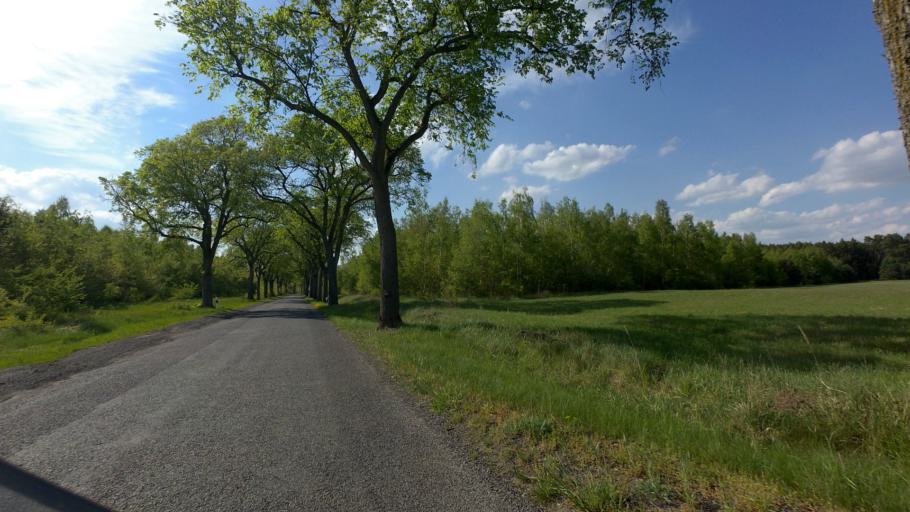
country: DE
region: Brandenburg
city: Templin
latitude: 53.0037
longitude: 13.4710
